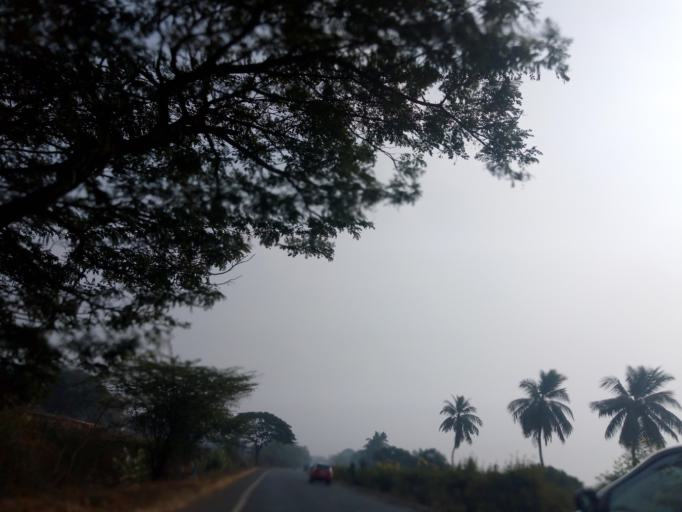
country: IN
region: Andhra Pradesh
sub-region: West Godavari
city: Tadepallegudem
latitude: 16.8182
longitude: 81.3903
